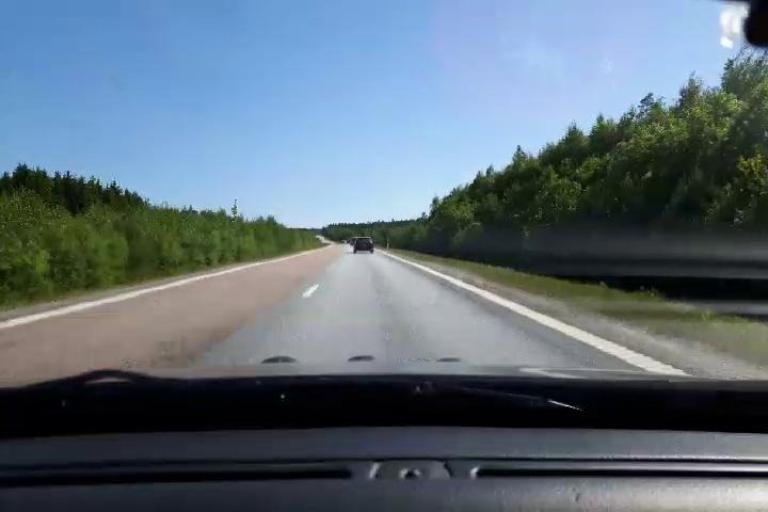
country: SE
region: Gaevleborg
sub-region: Hudiksvalls Kommun
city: Iggesund
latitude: 61.4852
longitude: 16.9843
